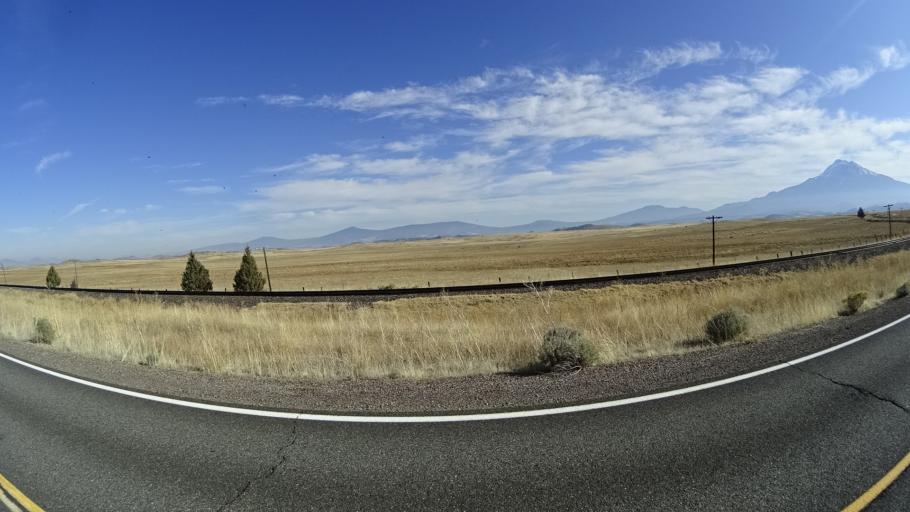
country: US
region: California
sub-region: Siskiyou County
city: Weed
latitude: 41.4941
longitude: -122.5102
